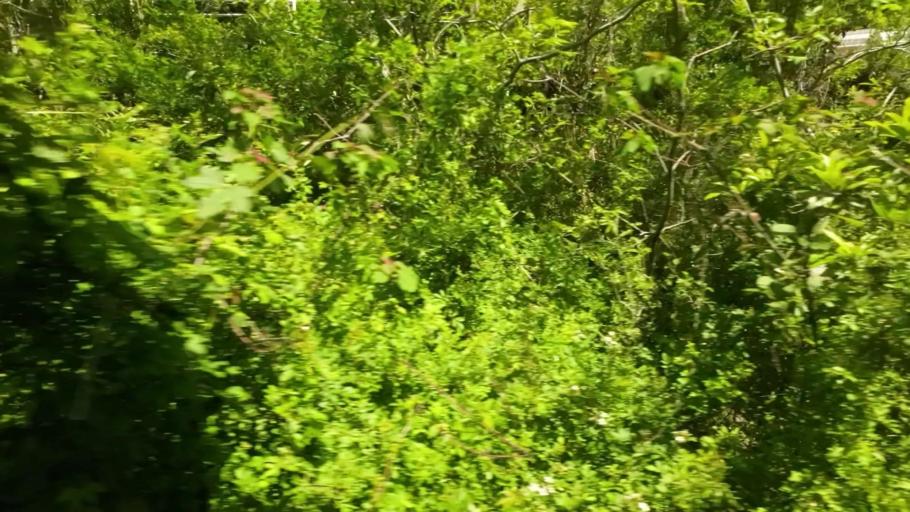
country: JP
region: Kochi
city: Kochi-shi
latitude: 33.6816
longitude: 133.6923
